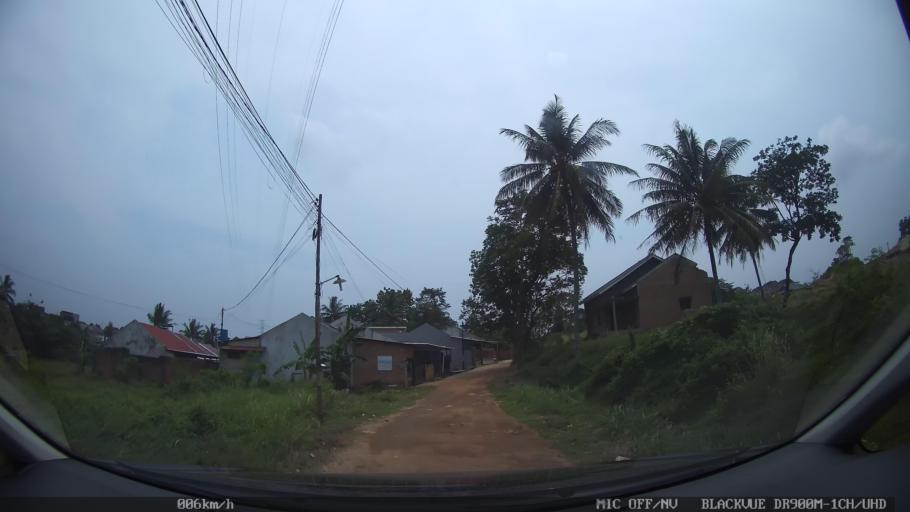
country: ID
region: Lampung
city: Kedaton
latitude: -5.4014
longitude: 105.3263
